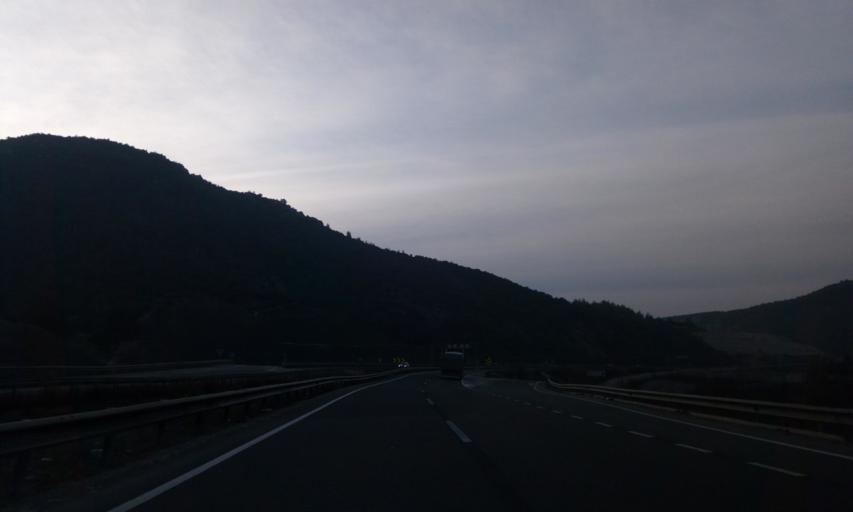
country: TR
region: Bilecik
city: Bilecik
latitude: 40.1655
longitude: 30.0208
